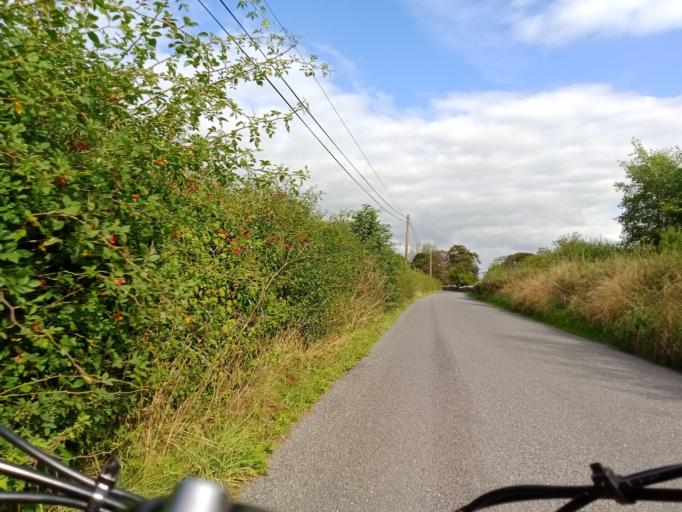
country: IE
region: Leinster
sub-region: Kilkenny
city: Kilkenny
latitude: 52.6073
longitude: -7.2205
